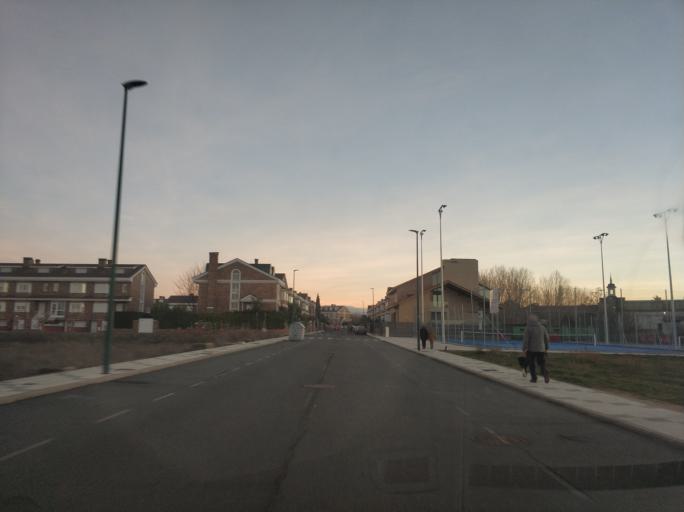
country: ES
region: Castille and Leon
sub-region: Provincia de Salamanca
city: Santa Marta de Tormes
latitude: 40.9540
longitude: -5.6460
